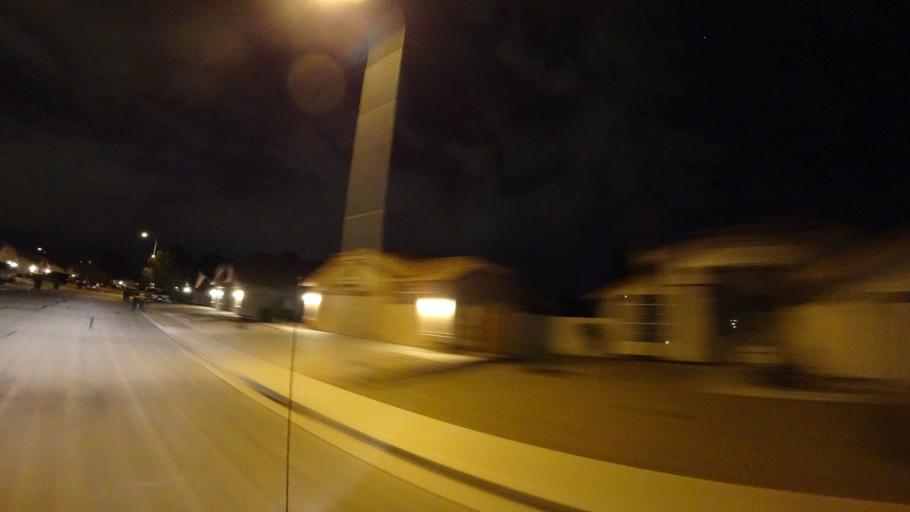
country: US
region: Arizona
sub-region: Maricopa County
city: Chandler
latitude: 33.2908
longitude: -111.8702
